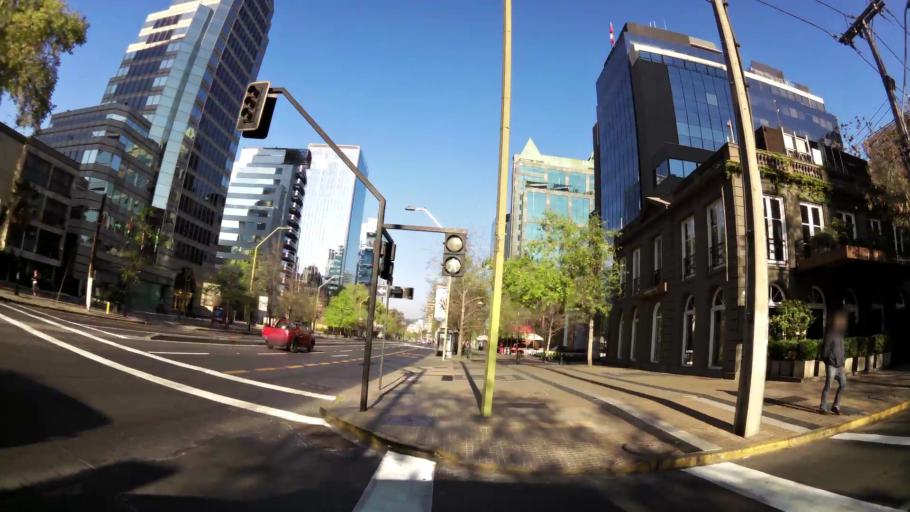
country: CL
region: Santiago Metropolitan
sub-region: Provincia de Santiago
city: Villa Presidente Frei, Nunoa, Santiago, Chile
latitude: -33.4168
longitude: -70.5975
